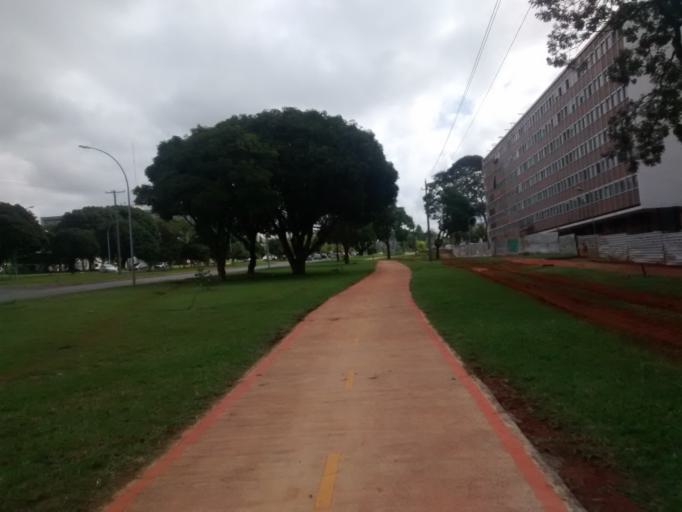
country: BR
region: Federal District
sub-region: Brasilia
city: Brasilia
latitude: -15.7832
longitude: -47.8852
